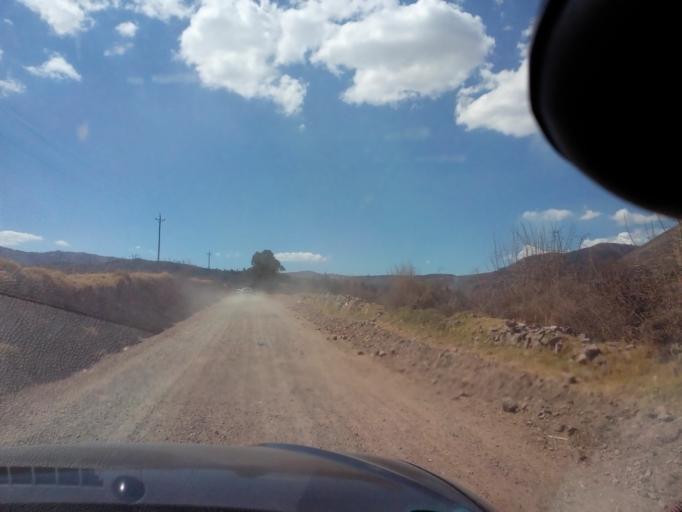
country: PE
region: Cusco
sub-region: Provincia de Anta
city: Huarocondo
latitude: -13.4214
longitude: -72.2123
